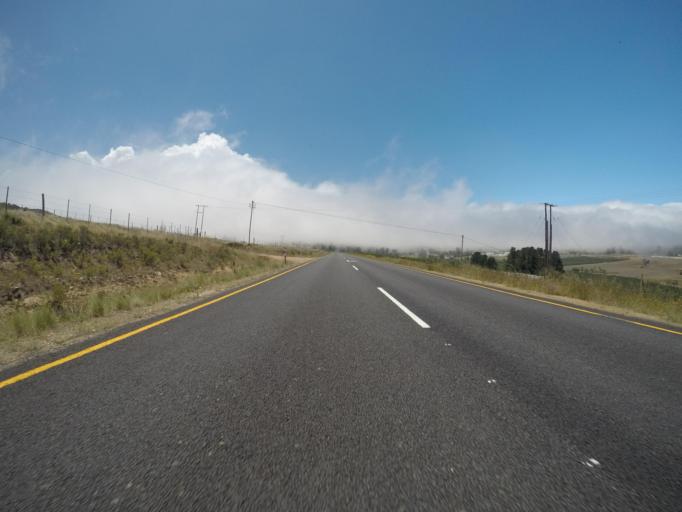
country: ZA
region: Western Cape
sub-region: Eden District Municipality
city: Knysna
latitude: -33.7269
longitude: 23.1531
